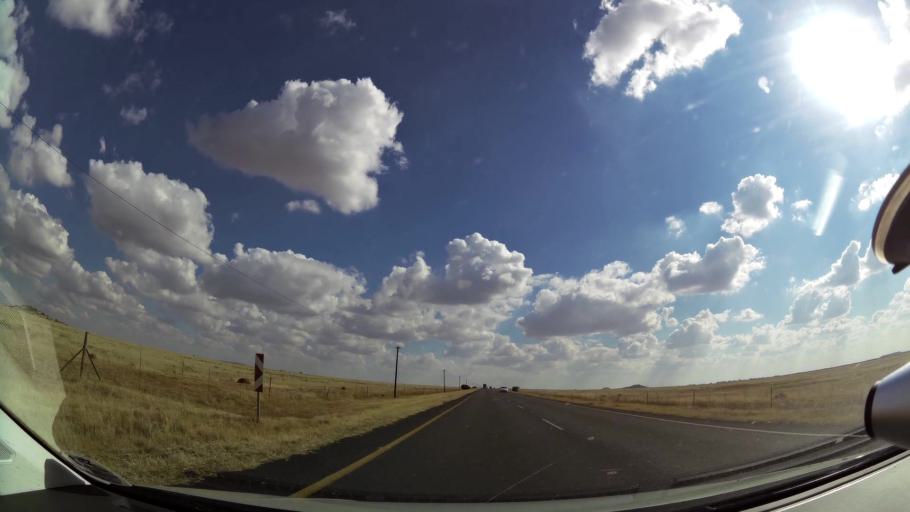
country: ZA
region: Orange Free State
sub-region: Mangaung Metropolitan Municipality
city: Bloemfontein
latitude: -29.1550
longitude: 25.7289
